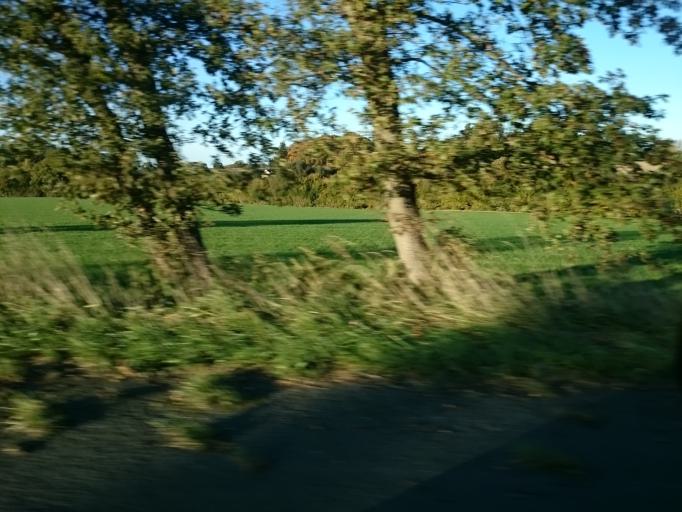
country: FR
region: Brittany
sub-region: Departement des Cotes-d'Armor
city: Plelo
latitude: 48.5289
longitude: -2.9068
